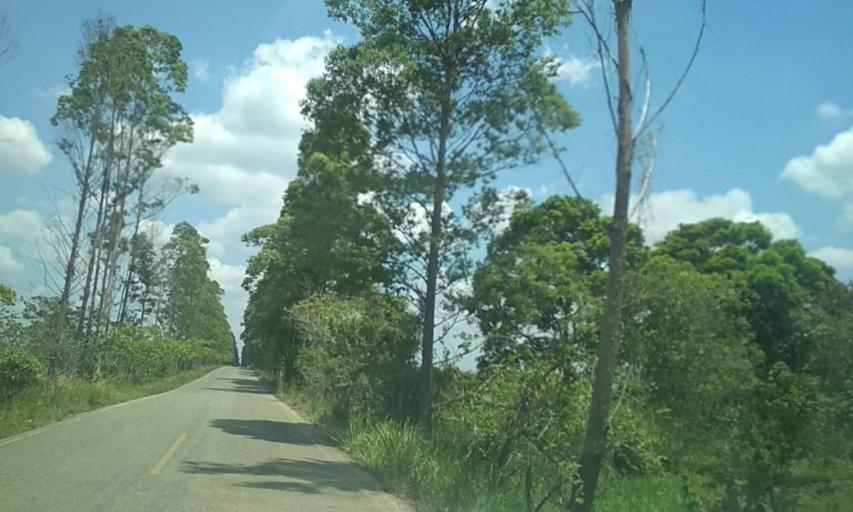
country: MX
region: Tabasco
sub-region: Huimanguillo
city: Francisco Rueda
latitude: 17.7659
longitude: -93.7952
